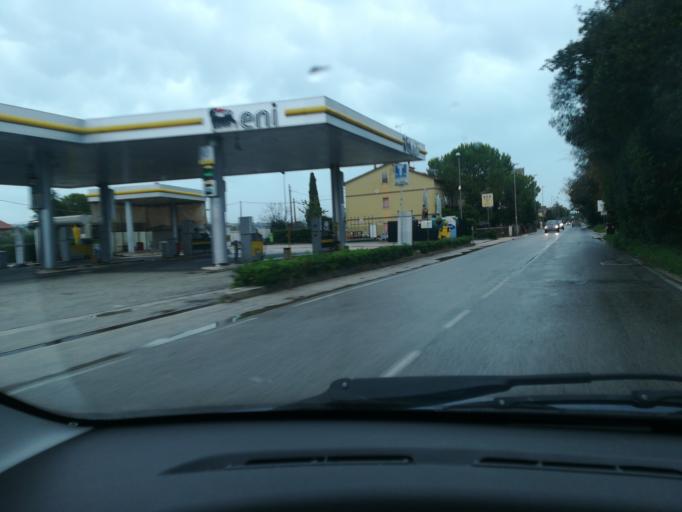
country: IT
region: The Marches
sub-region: Provincia di Macerata
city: Borgo Stazione
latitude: 43.2814
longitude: 13.6302
